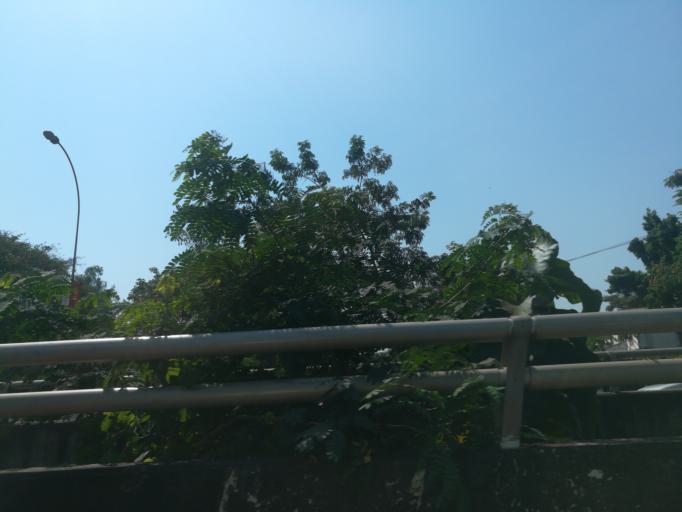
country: NG
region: Abuja Federal Capital Territory
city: Abuja
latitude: 9.0549
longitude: 7.4580
